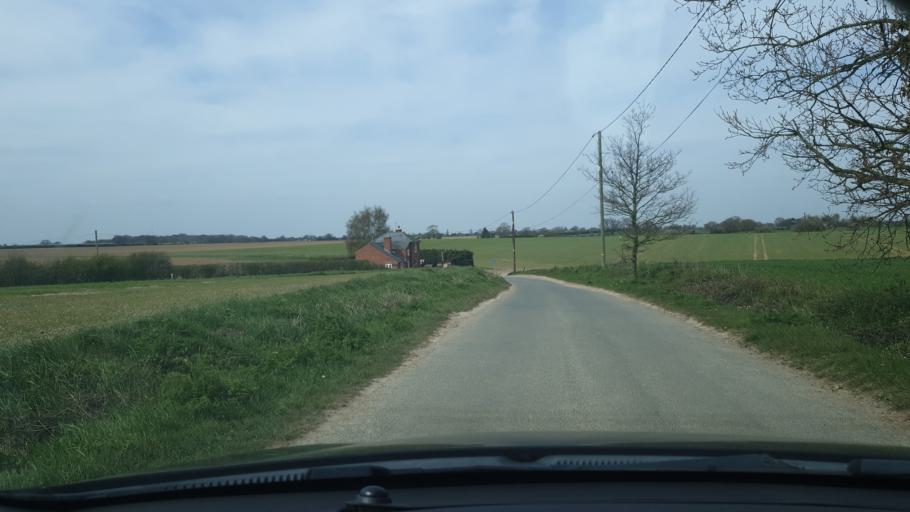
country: GB
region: England
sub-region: Essex
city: Little Clacton
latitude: 51.8991
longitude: 1.1668
